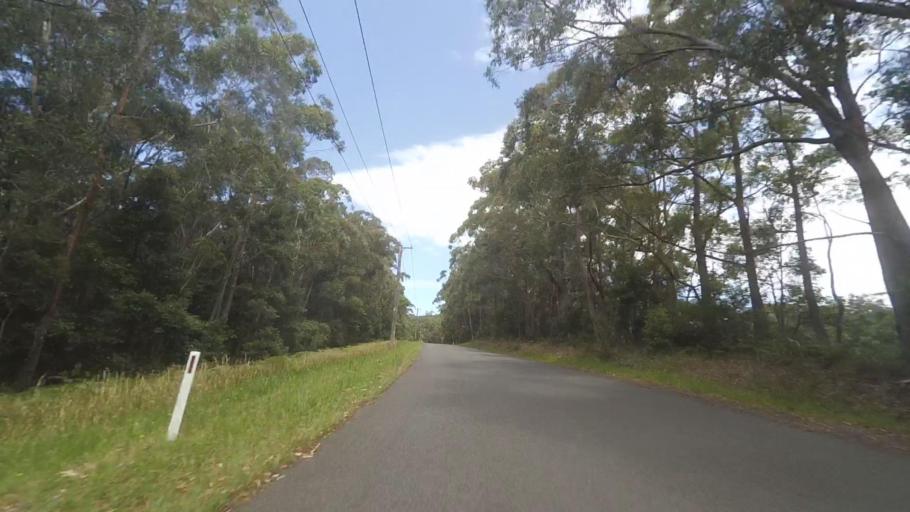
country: AU
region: New South Wales
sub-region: Shoalhaven Shire
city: Milton
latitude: -35.3902
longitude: 150.3669
